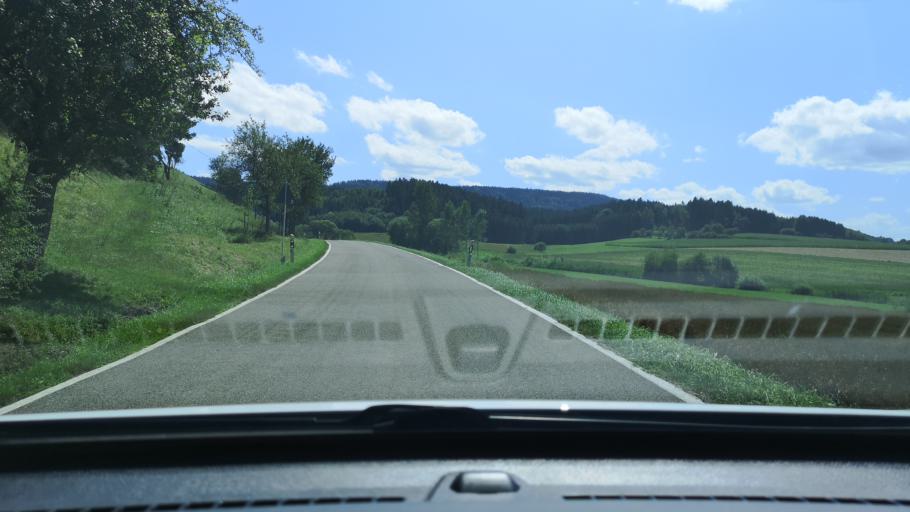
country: DE
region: Baden-Wuerttemberg
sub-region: Freiburg Region
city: Muhlheim am Bach
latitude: 48.3655
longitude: 8.7093
